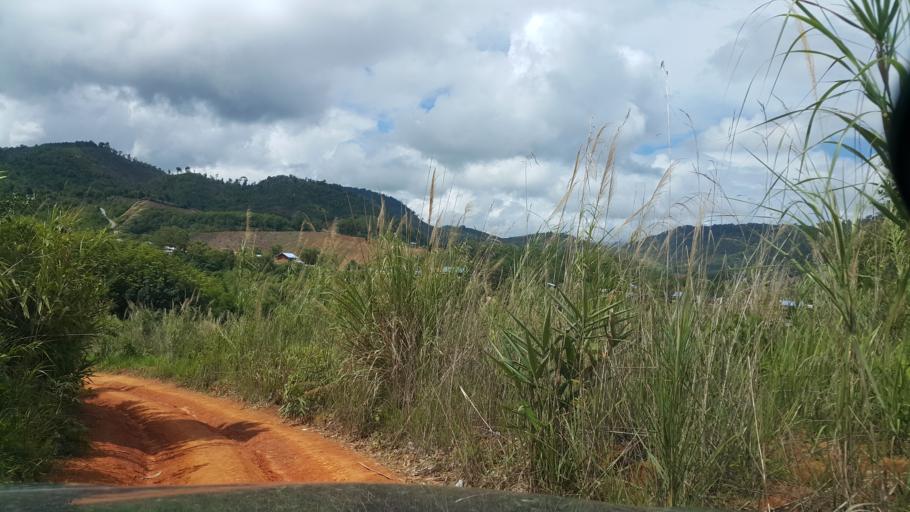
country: TH
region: Loei
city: Na Haeo
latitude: 17.5958
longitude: 100.9006
